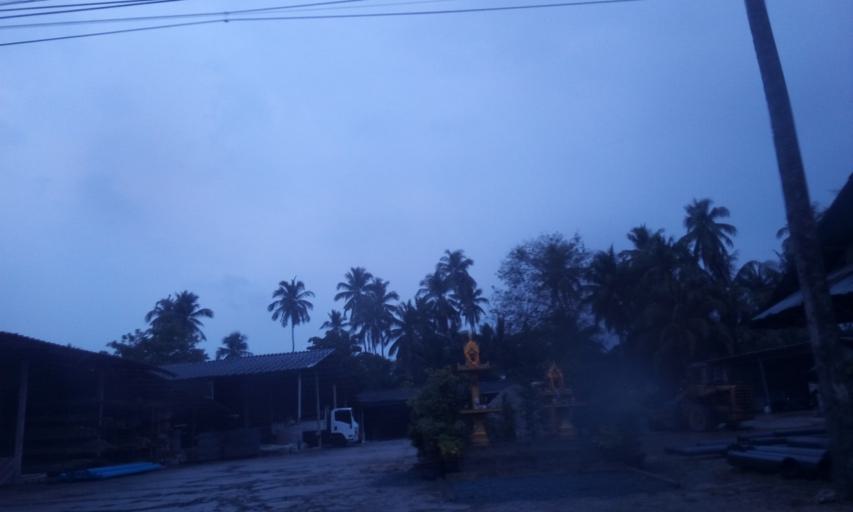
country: TH
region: Trat
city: Laem Ngop
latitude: 12.1338
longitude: 102.2759
